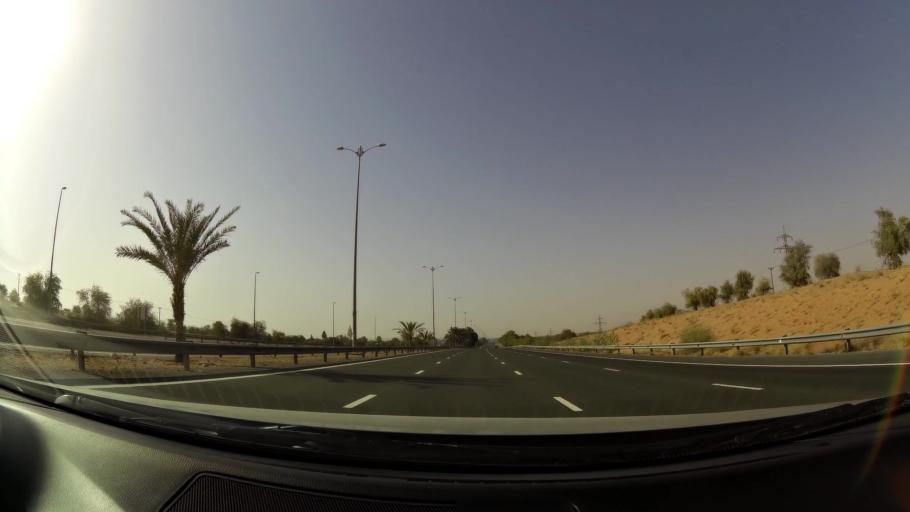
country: OM
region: Al Buraimi
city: Al Buraymi
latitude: 24.6159
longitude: 55.7275
